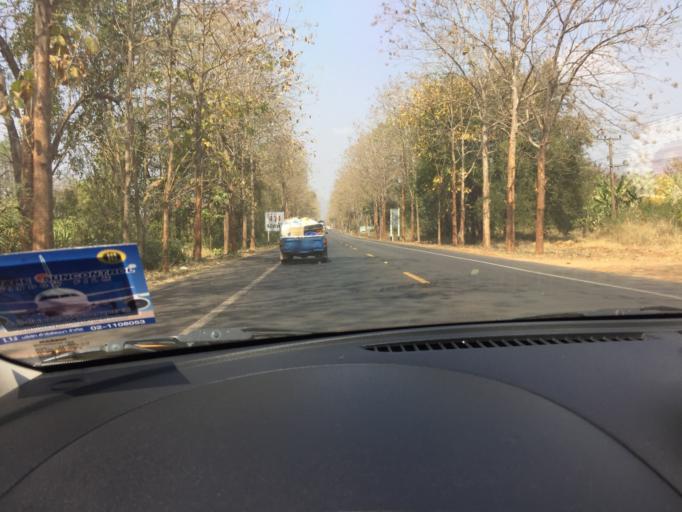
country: TH
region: Kanchanaburi
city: Sai Yok
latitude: 14.1771
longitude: 99.1274
